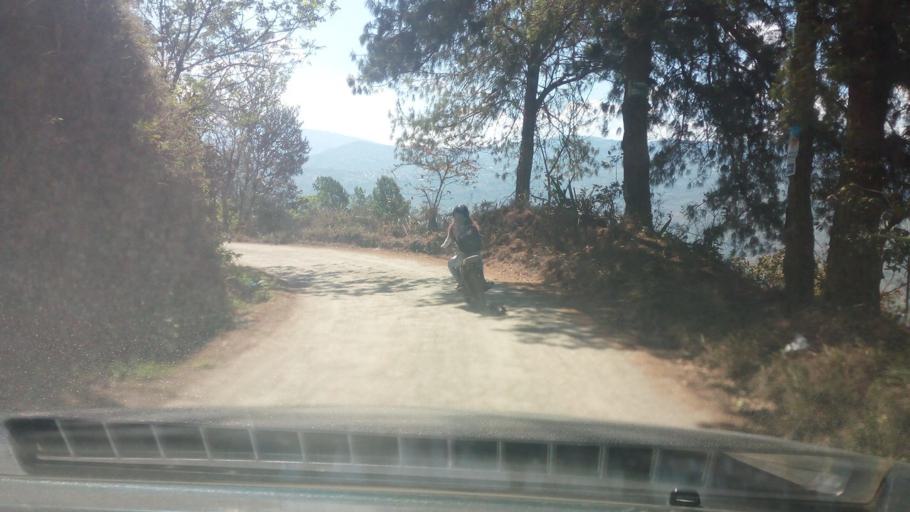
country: CO
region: Boyaca
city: Somondoco
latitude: 4.9862
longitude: -73.4253
